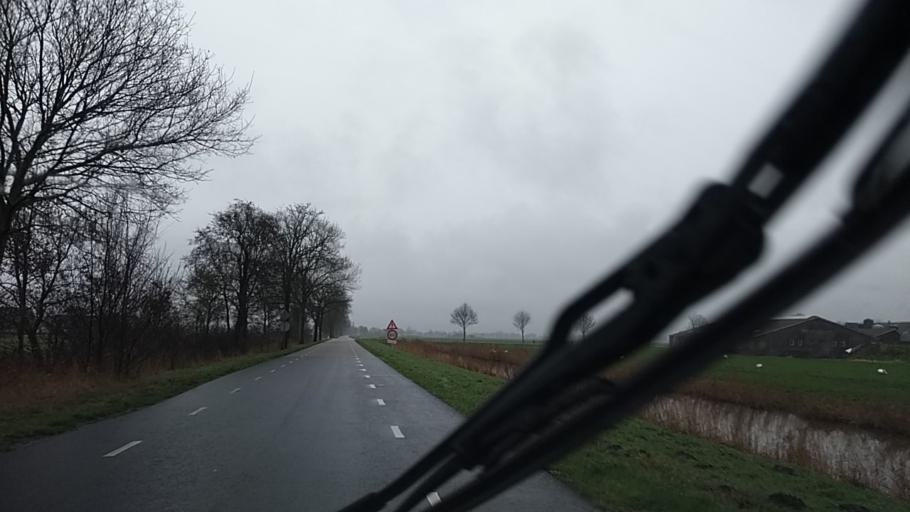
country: NL
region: Overijssel
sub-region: Gemeente Staphorst
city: Staphorst
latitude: 52.6107
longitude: 6.1573
